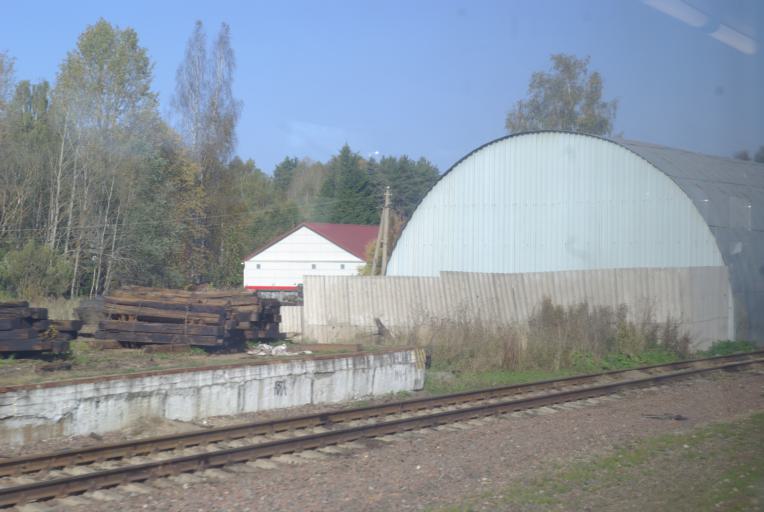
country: RU
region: Moskovskaya
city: Novo-Nikol'skoye
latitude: 56.5375
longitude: 37.5599
